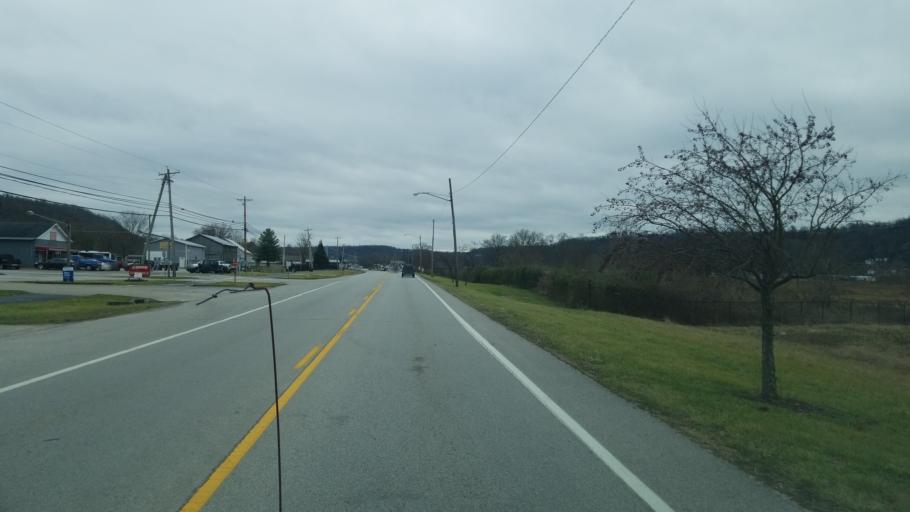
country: US
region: Ohio
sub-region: Brown County
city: Aberdeen
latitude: 38.6657
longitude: -83.7708
